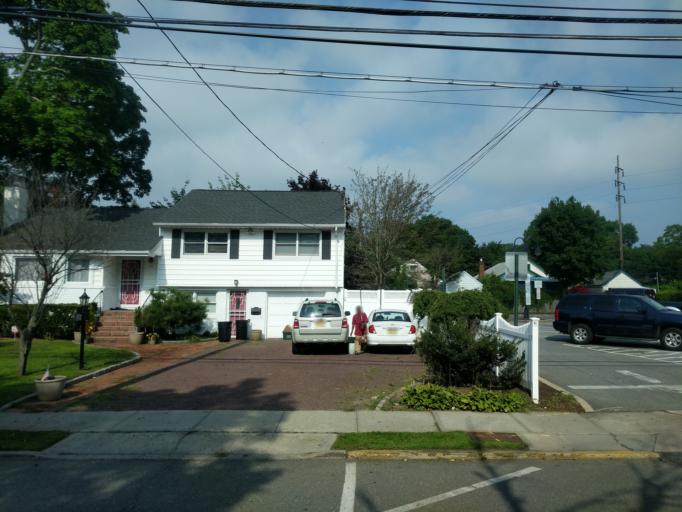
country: US
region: New York
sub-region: Nassau County
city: Malverne
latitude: 40.6739
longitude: -73.6702
